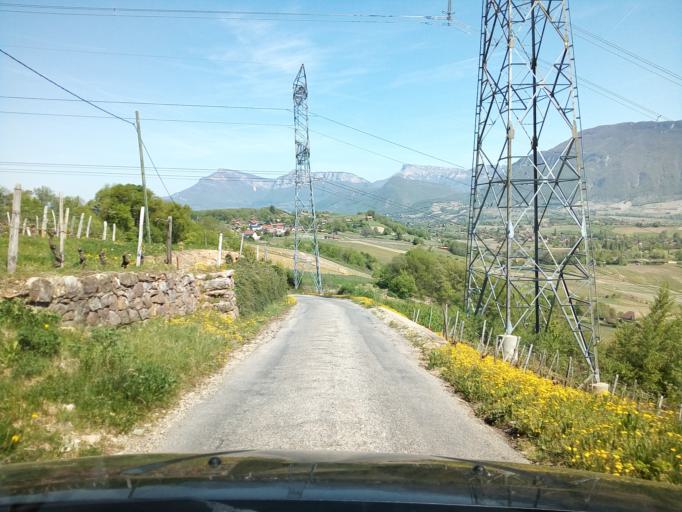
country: FR
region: Rhone-Alpes
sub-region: Departement de l'Isere
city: Chapareillan
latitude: 45.4832
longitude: 5.9779
